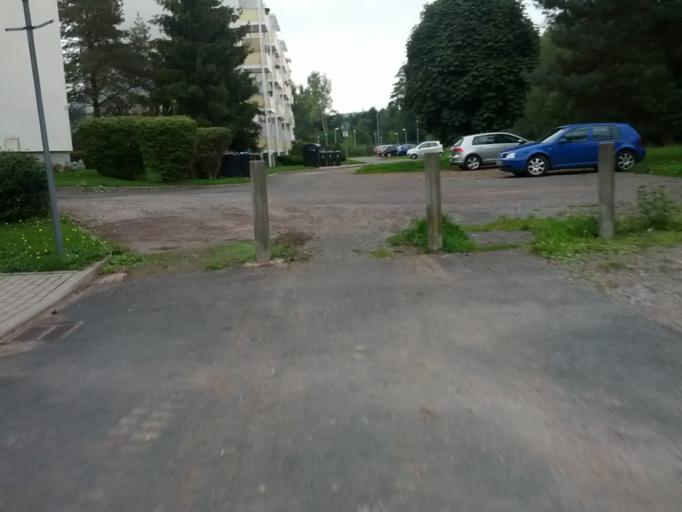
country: DE
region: Thuringia
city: Thal
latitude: 50.9518
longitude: 10.3882
